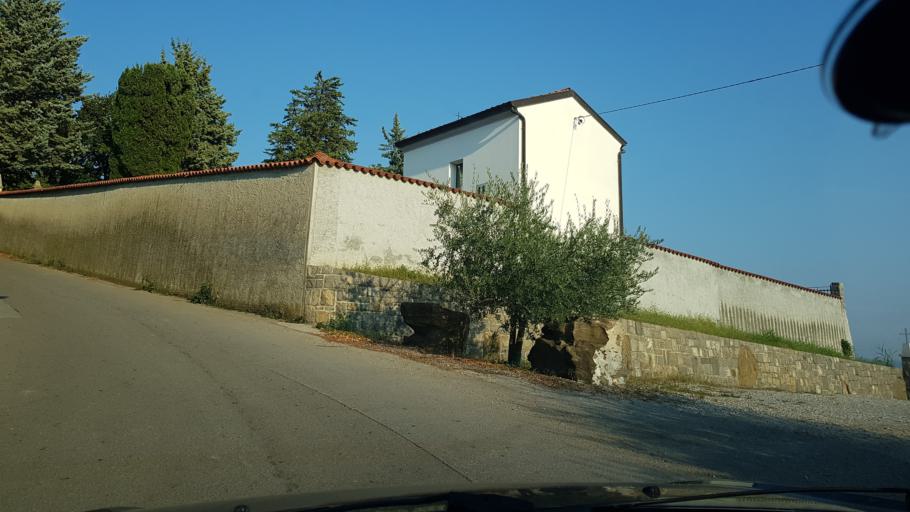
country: IT
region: Friuli Venezia Giulia
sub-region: Provincia di Gorizia
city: San Floriano del Collio
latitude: 45.9809
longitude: 13.5612
